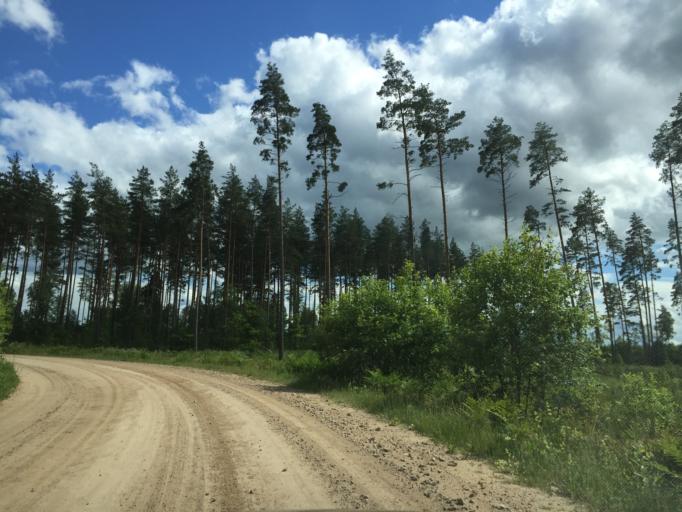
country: LV
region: Vecumnieki
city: Vecumnieki
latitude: 56.4865
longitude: 24.4094
